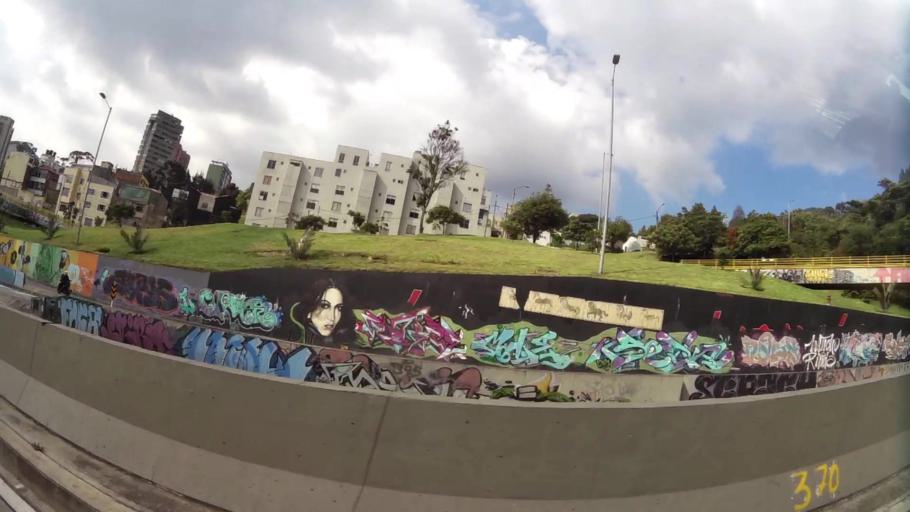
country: CO
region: Bogota D.C.
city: Bogota
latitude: 4.6089
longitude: -74.0667
